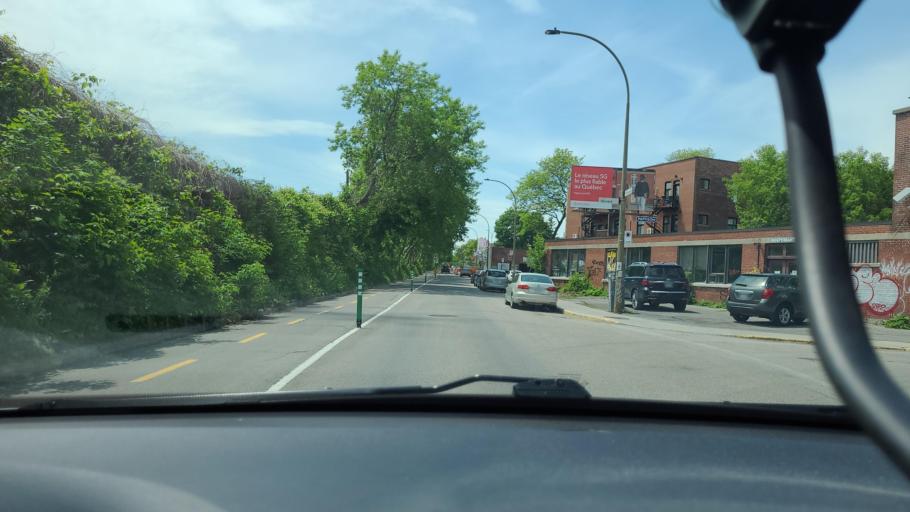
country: CA
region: Quebec
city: Saint-Raymond
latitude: 45.4693
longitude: -73.6119
